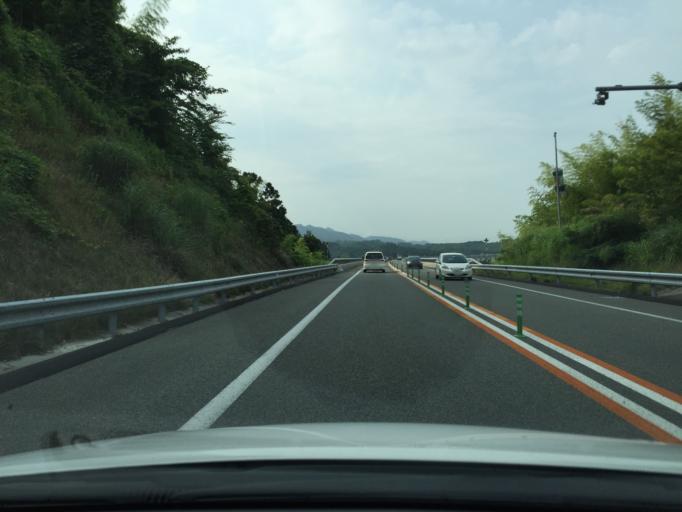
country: JP
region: Fukushima
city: Namie
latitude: 37.2708
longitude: 140.9845
